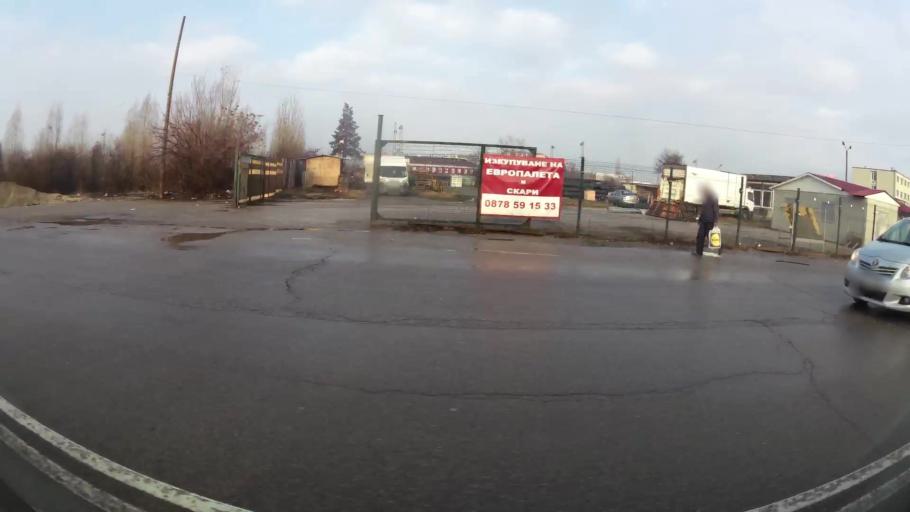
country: BG
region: Sofia-Capital
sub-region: Stolichna Obshtina
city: Sofia
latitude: 42.7301
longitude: 23.3199
